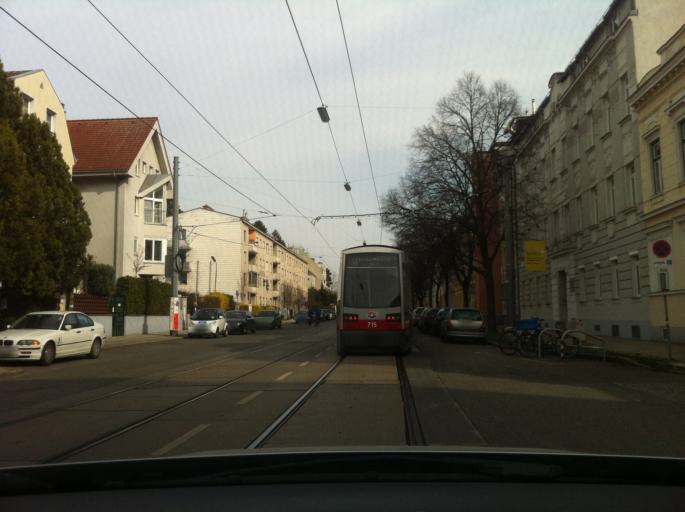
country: AT
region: Lower Austria
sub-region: Politischer Bezirk Modling
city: Perchtoldsdorf
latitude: 48.1986
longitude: 16.2733
